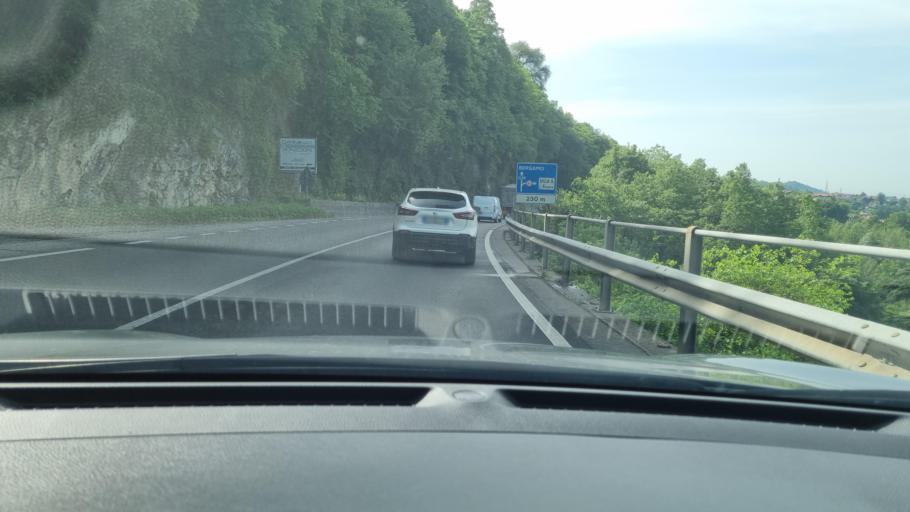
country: IT
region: Lombardy
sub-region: Provincia di Bergamo
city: Villa d'Alme
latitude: 45.7594
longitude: 9.6085
